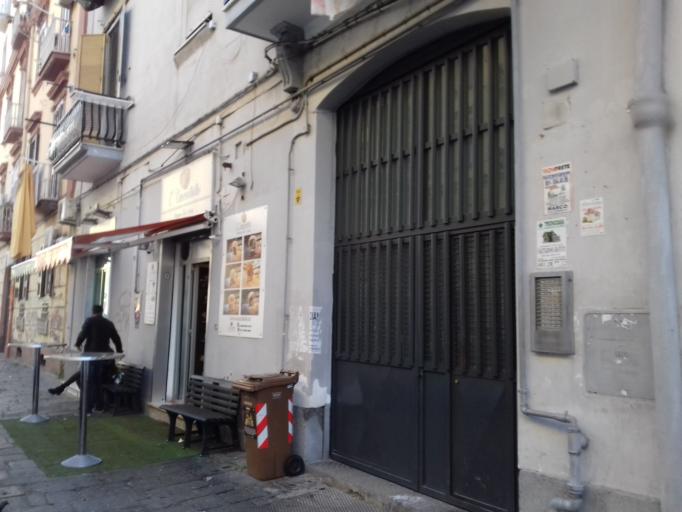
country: IT
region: Campania
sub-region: Provincia di Napoli
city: Napoli
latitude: 40.8576
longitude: 14.2747
